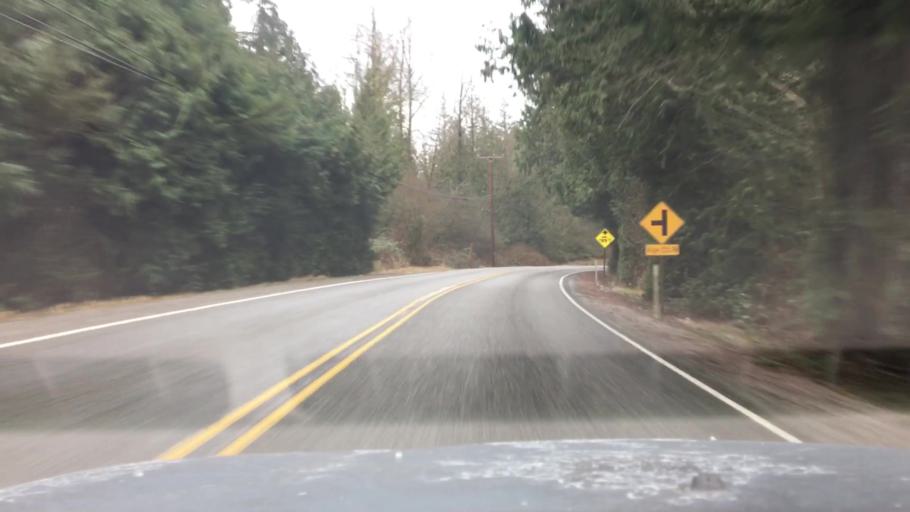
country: US
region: Washington
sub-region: Whatcom County
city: Sudden Valley
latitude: 48.6361
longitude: -122.3113
